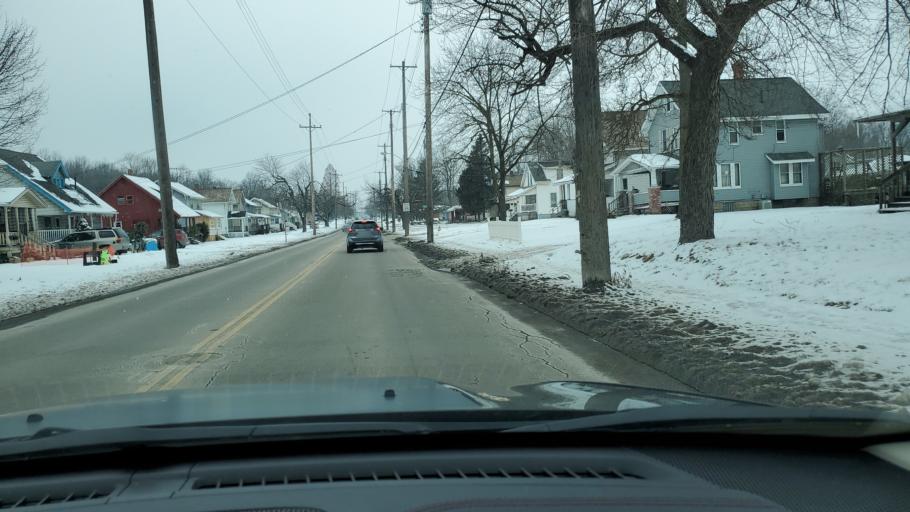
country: US
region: Ohio
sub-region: Trumbull County
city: Warren
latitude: 41.2422
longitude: -80.8387
